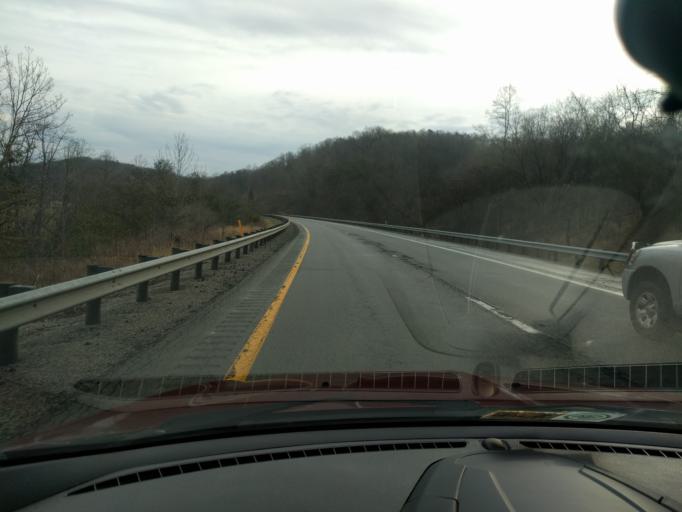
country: US
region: West Virginia
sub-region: Jackson County
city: Ravenswood
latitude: 38.9872
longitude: -81.6775
